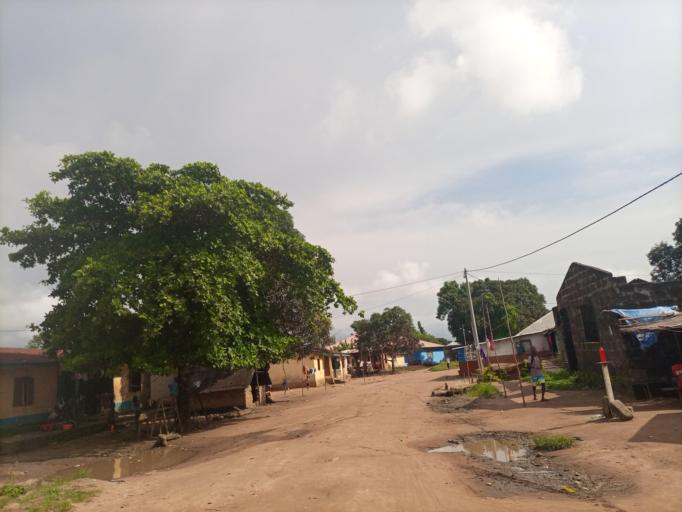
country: SL
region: Northern Province
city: Masoyila
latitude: 8.6109
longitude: -13.1717
